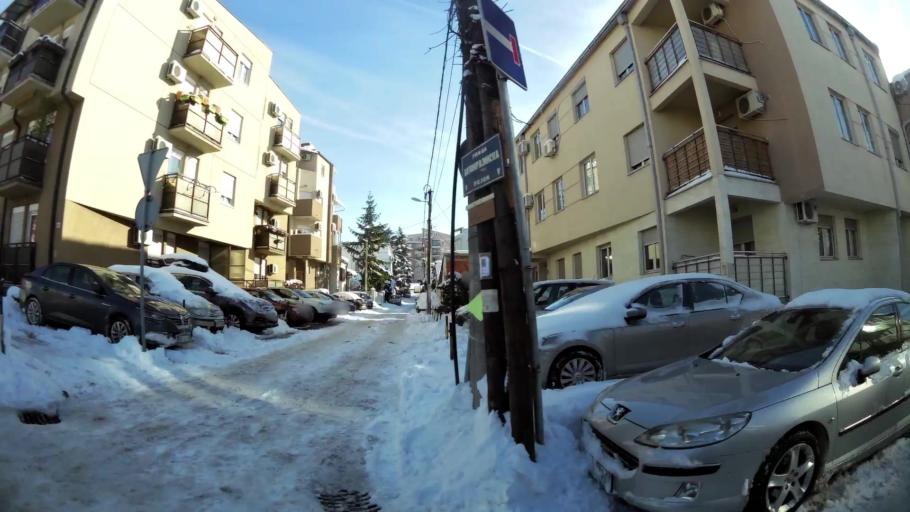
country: RS
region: Central Serbia
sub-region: Belgrade
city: Palilula
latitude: 44.7894
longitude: 20.5062
